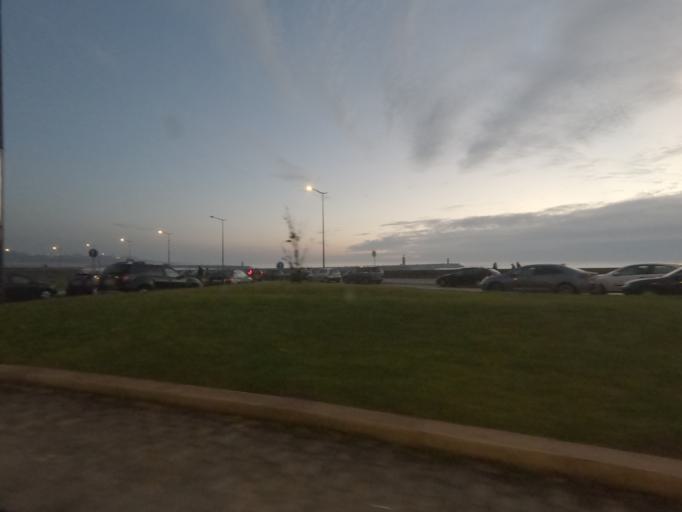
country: PT
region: Porto
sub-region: Matosinhos
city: Matosinhos
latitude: 41.1495
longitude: -8.6757
